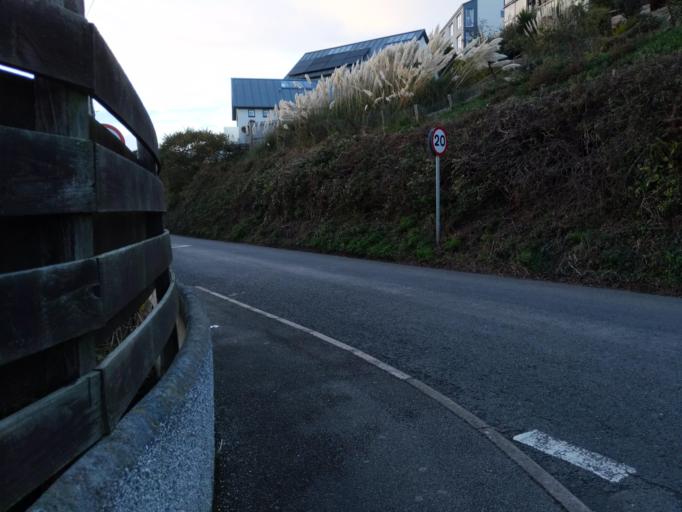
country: GB
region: England
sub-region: Cornwall
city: Looe
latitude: 50.3613
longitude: -4.3628
